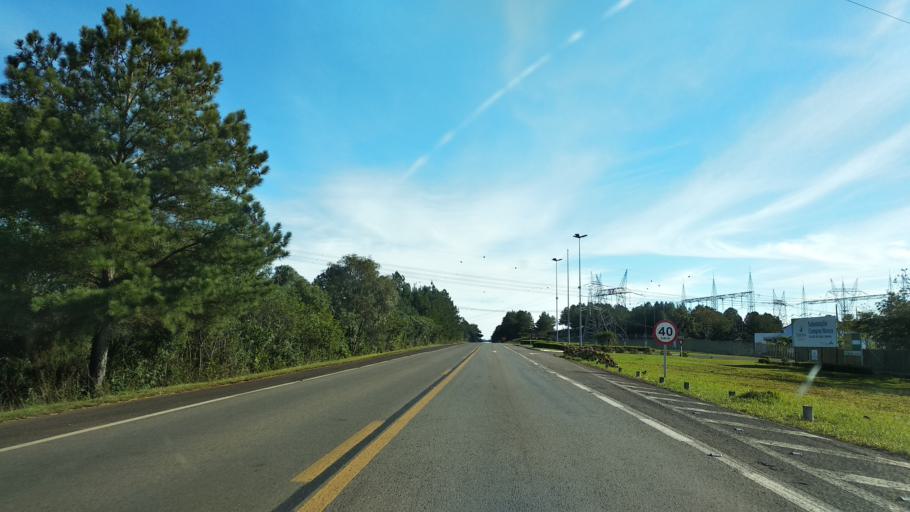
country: BR
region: Santa Catarina
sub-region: Celso Ramos
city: Celso Ramos
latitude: -27.5409
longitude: -51.4148
